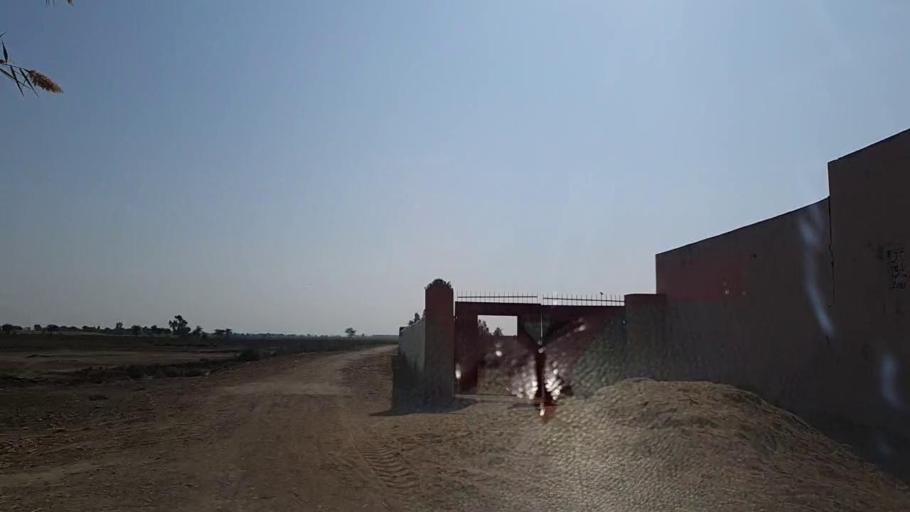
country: PK
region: Sindh
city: Sanghar
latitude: 25.9849
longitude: 69.0614
